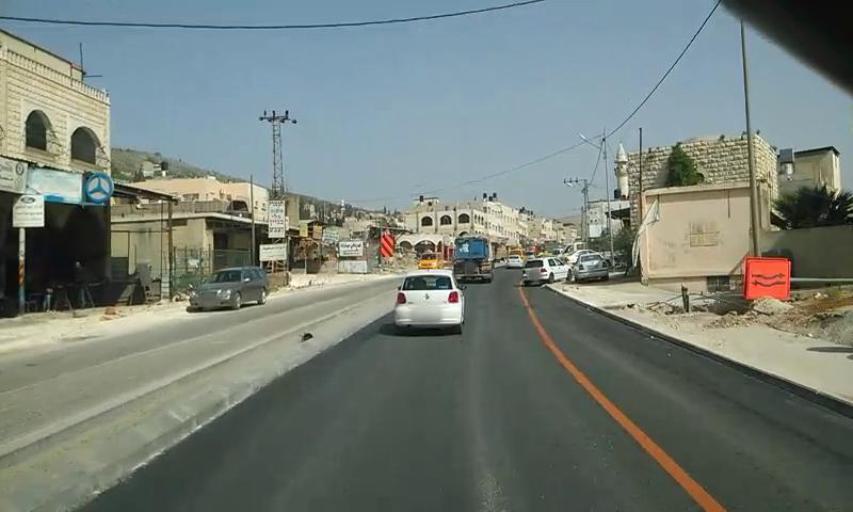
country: PS
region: West Bank
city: Huwwarah
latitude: 32.1481
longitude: 35.2578
